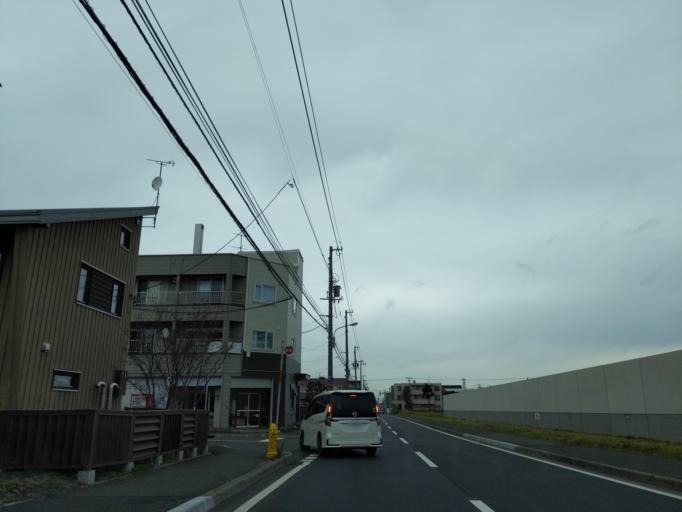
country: JP
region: Hokkaido
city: Sapporo
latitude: 43.0850
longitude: 141.3961
